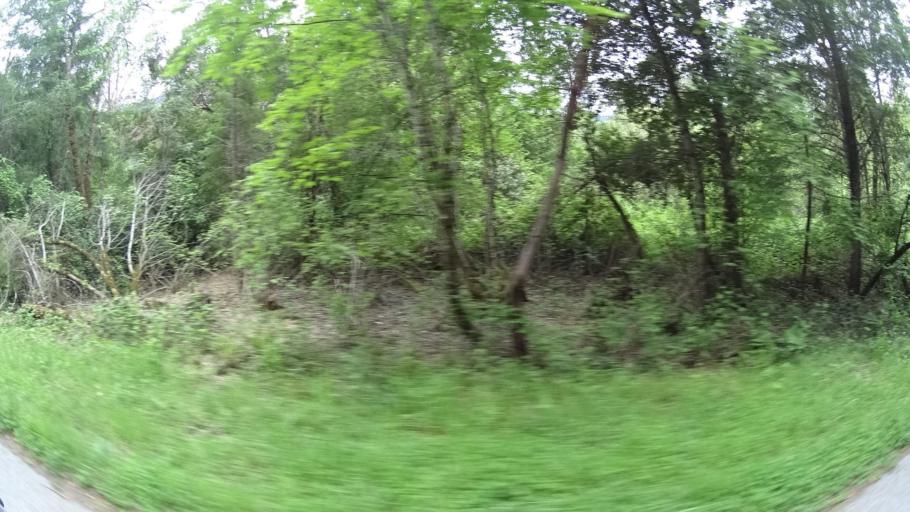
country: US
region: California
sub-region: Humboldt County
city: Willow Creek
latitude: 40.9675
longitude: -123.6336
